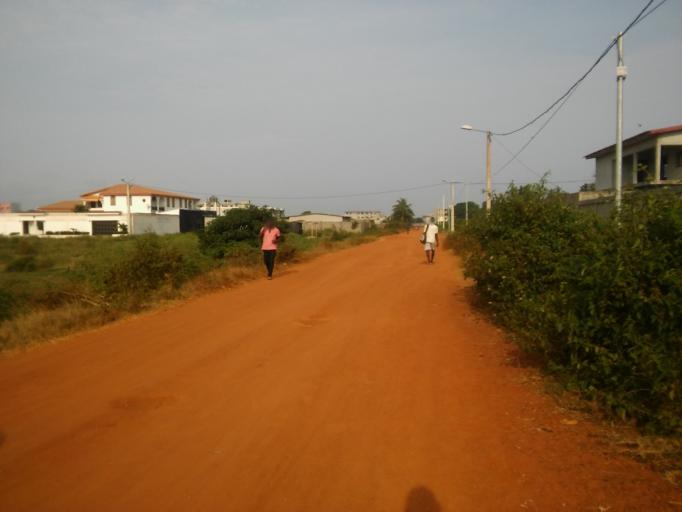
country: CI
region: Sud-Comoe
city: Grand-Bassam
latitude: 5.2133
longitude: -3.7648
